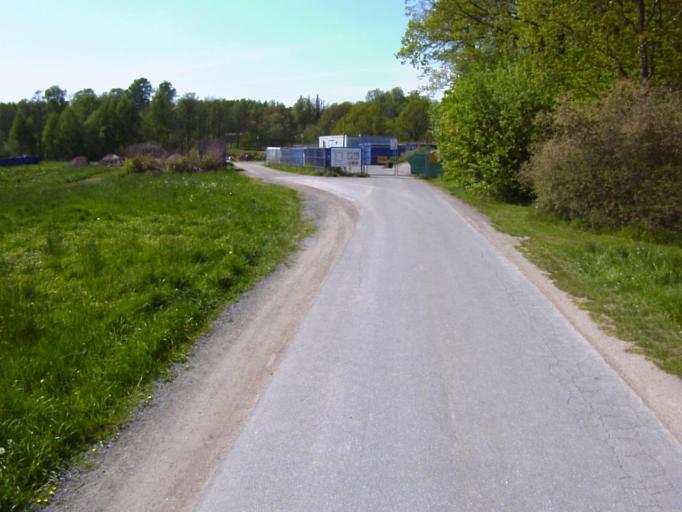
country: SE
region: Skane
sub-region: Kristianstads Kommun
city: Tollarp
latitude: 56.1703
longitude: 14.2872
